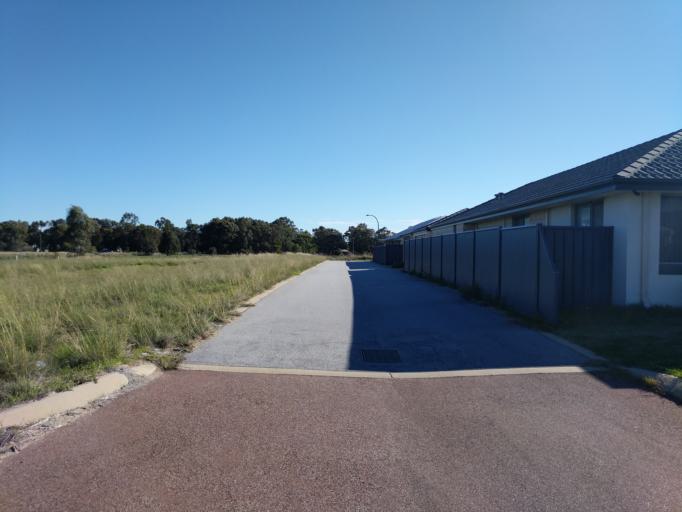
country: AU
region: Western Australia
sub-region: Serpentine-Jarrahdale
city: Byford
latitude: -32.2219
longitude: 115.9756
